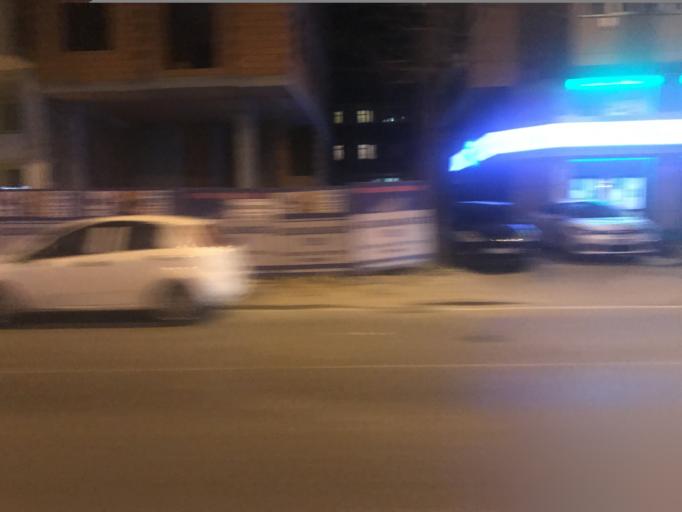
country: TR
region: Istanbul
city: Bahcelievler
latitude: 40.9837
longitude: 28.8725
